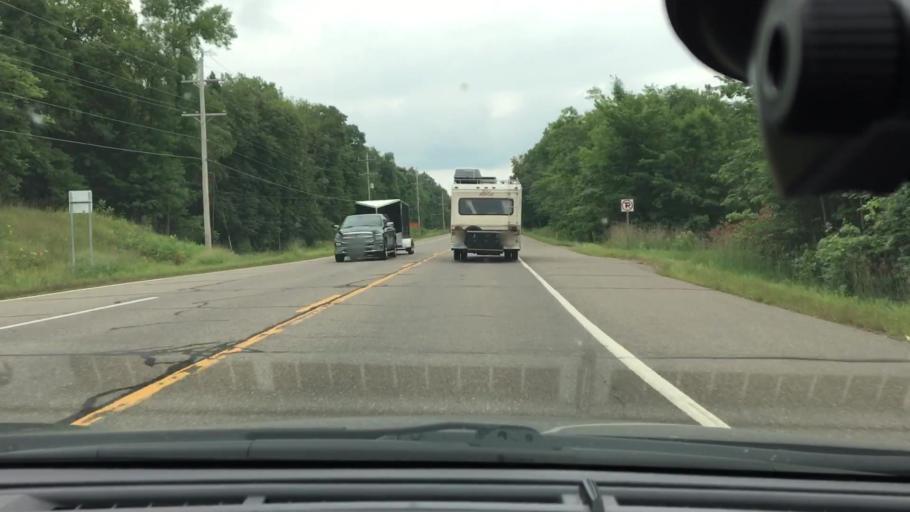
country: US
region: Minnesota
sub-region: Crow Wing County
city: Crosby
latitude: 46.4909
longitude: -93.9152
